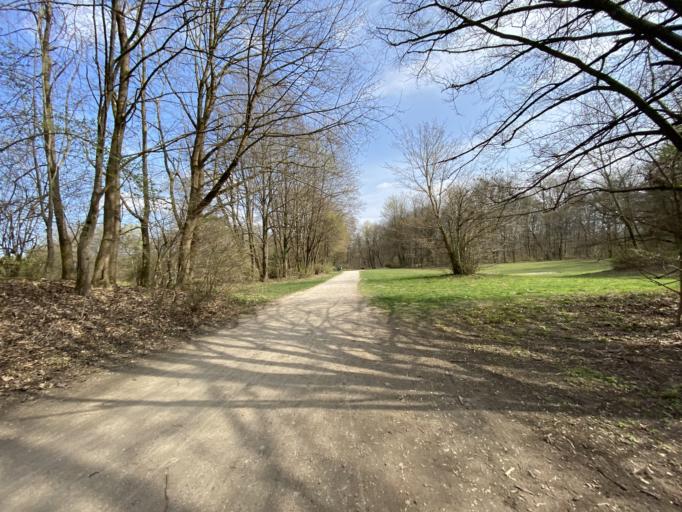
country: DE
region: Bavaria
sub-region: Upper Bavaria
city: Bogenhausen
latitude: 48.1808
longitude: 11.6129
